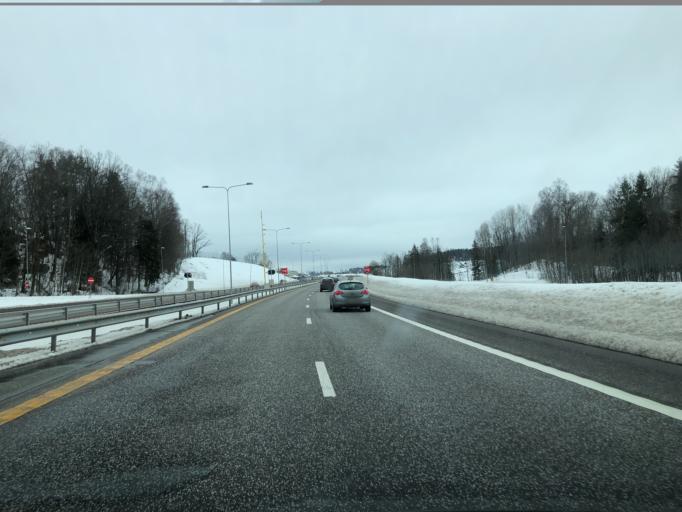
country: NO
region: Vestfold
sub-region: Holmestrand
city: Holmestrand
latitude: 59.4486
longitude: 10.3562
